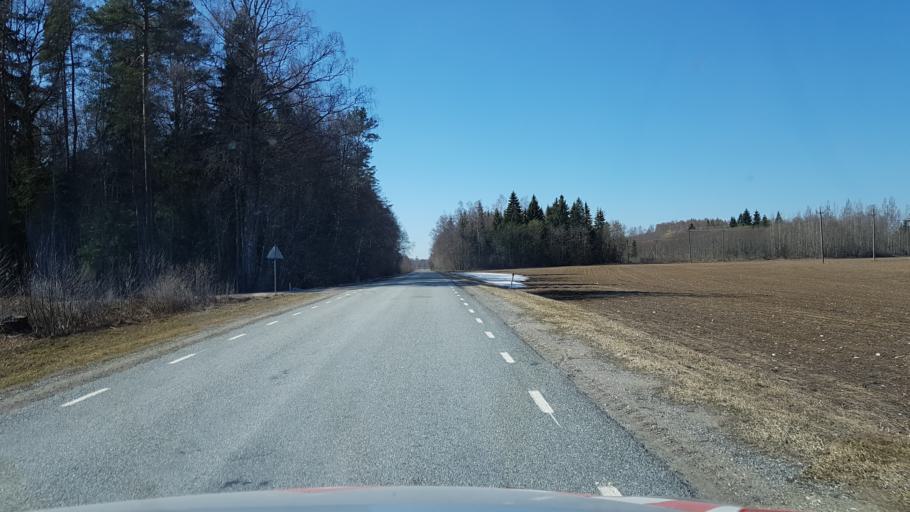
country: EE
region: Laeaene-Virumaa
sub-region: Vaeike-Maarja vald
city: Vaike-Maarja
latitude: 59.1236
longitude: 26.3053
